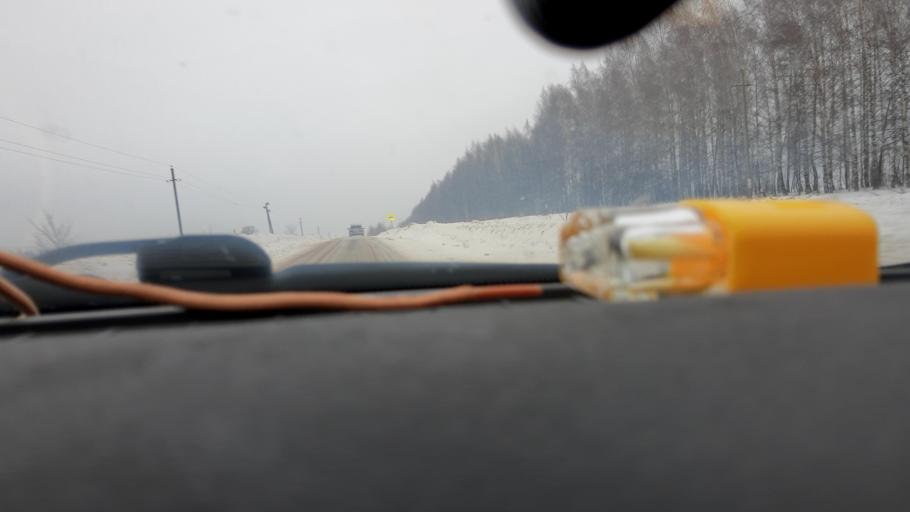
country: RU
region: Bashkortostan
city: Ulukulevo
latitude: 54.5663
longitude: 56.4316
